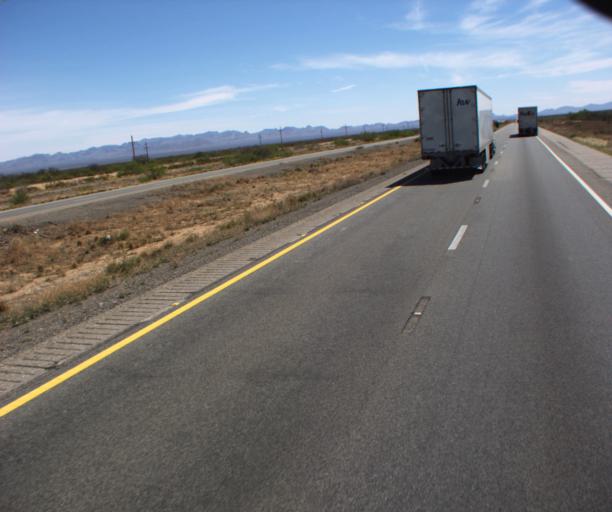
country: US
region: Arizona
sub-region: Cochise County
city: Willcox
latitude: 32.3007
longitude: -109.3694
